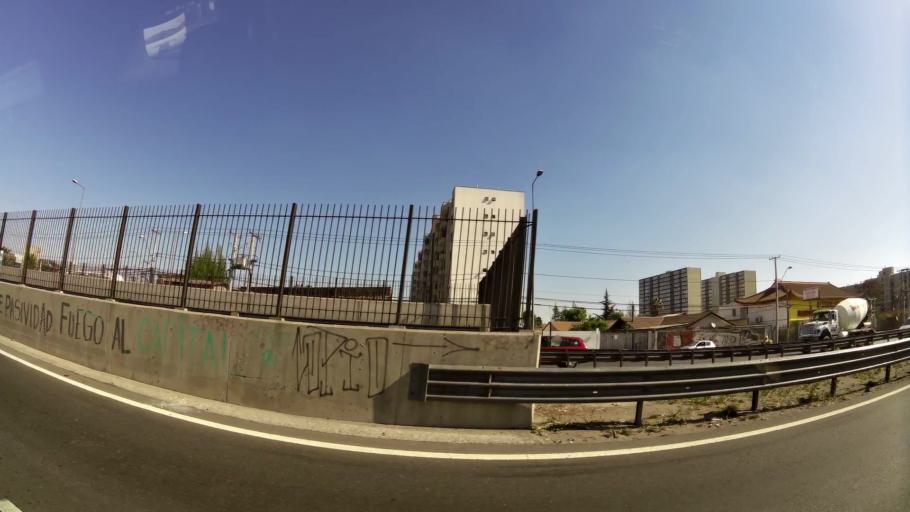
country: CL
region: Santiago Metropolitan
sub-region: Provincia de Santiago
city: La Pintana
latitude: -33.5358
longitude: -70.6692
